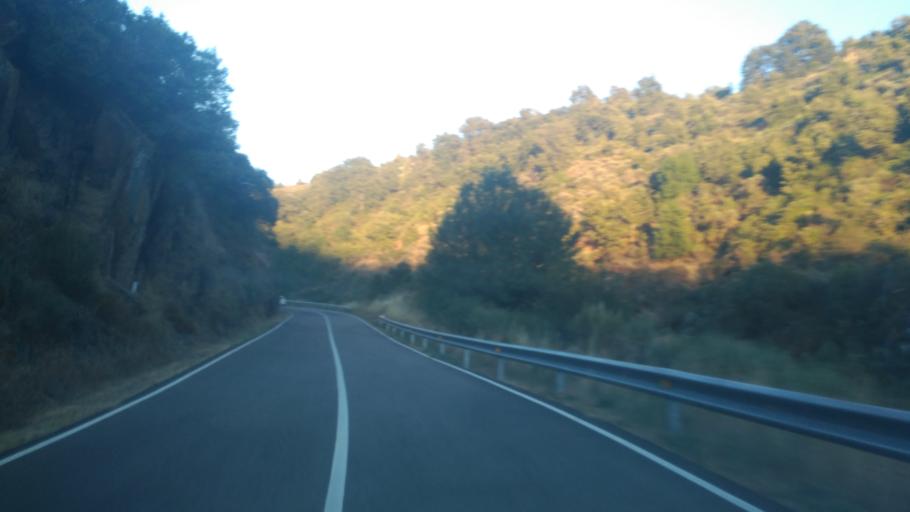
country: ES
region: Castille and Leon
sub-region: Provincia de Salamanca
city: Mieza
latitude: 41.1845
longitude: -6.6604
